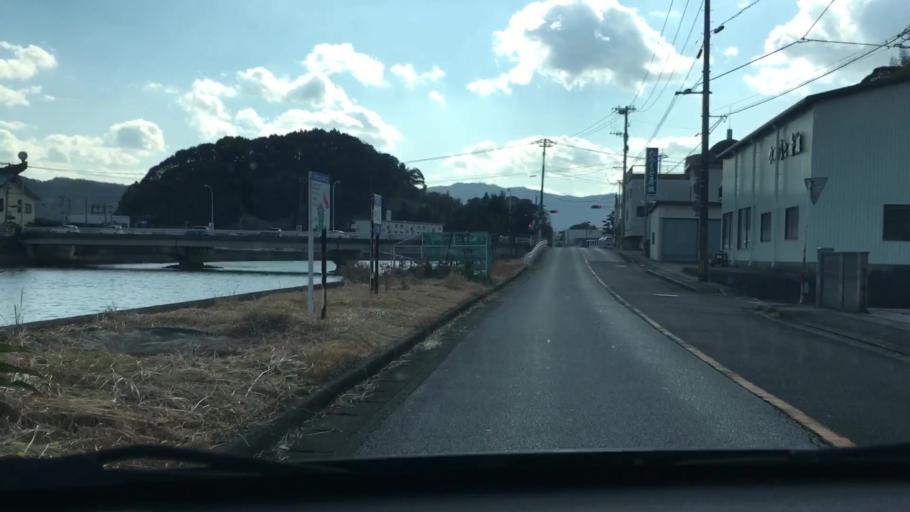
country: JP
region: Oita
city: Saiki
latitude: 32.9626
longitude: 131.9126
